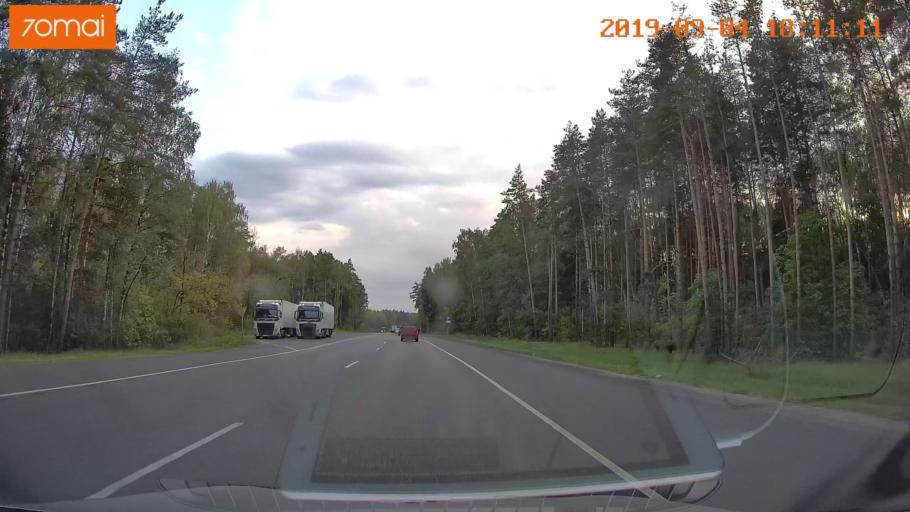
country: RU
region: Moskovskaya
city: Lopatinskiy
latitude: 55.3804
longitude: 38.7570
